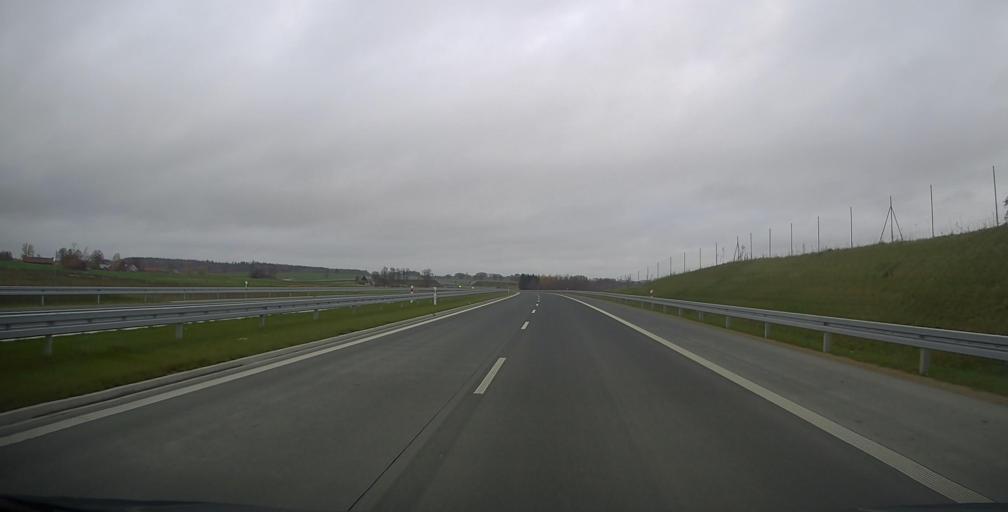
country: PL
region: Podlasie
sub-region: Powiat grajewski
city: Rajgrod
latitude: 53.8756
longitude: 22.6544
